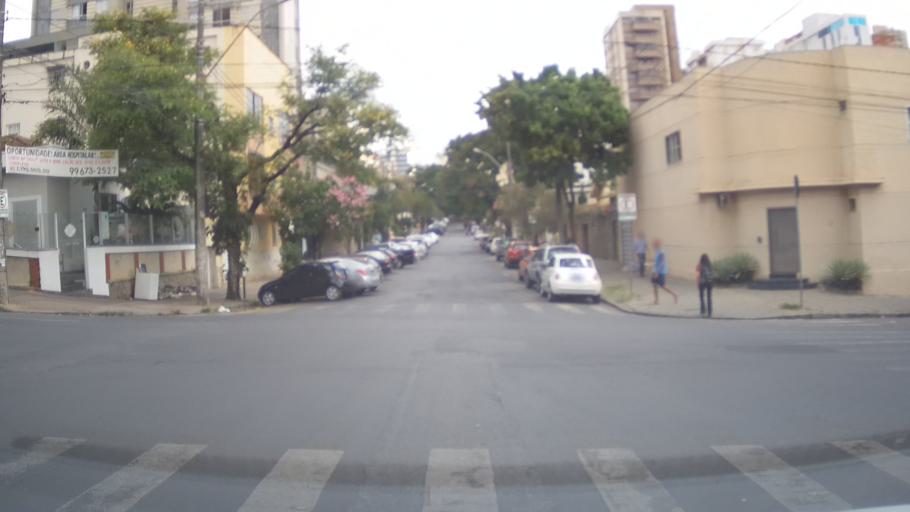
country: BR
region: Minas Gerais
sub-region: Belo Horizonte
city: Belo Horizonte
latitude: -19.9270
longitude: -43.9215
